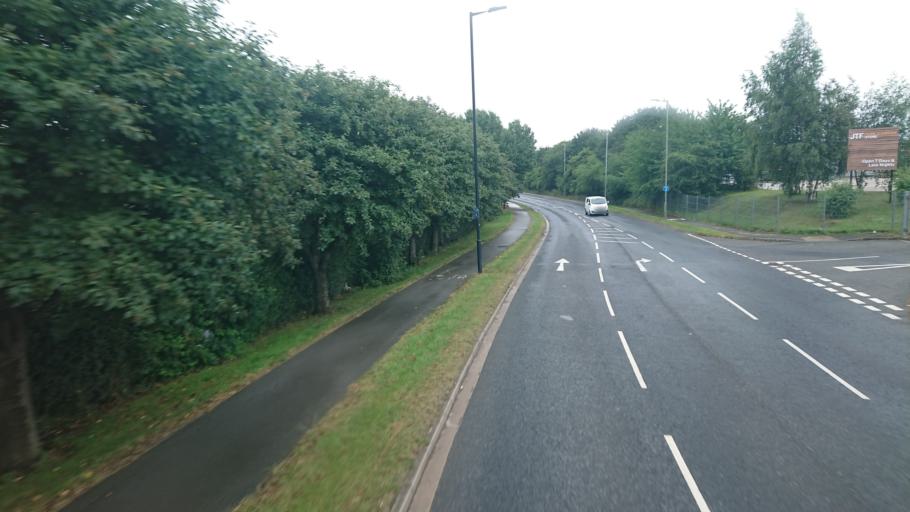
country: GB
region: England
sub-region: Rotherham
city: Orgreave
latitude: 53.3891
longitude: -1.3692
